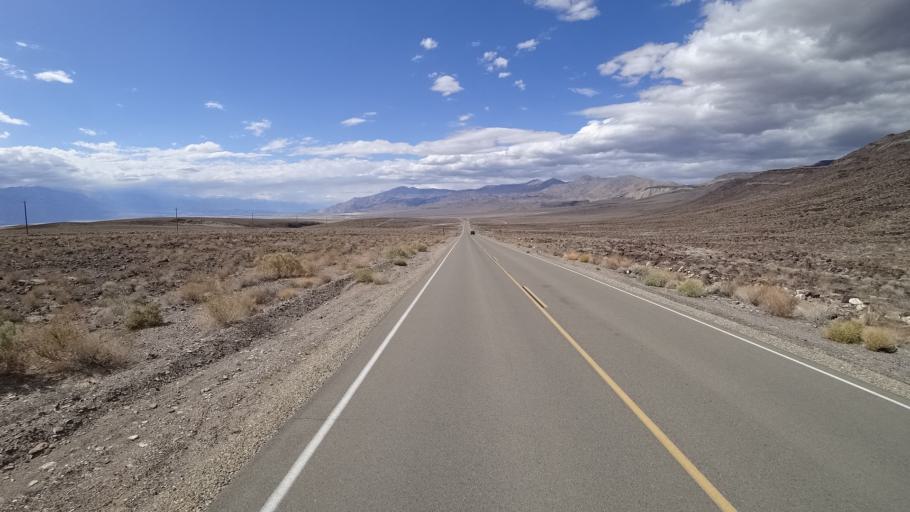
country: US
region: California
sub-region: Inyo County
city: Lone Pine
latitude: 36.3969
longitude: -117.8081
